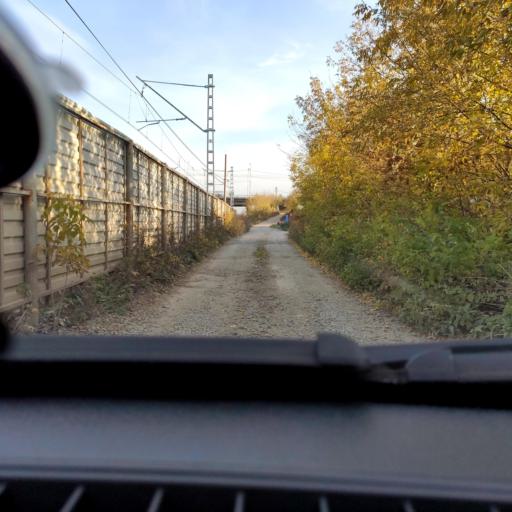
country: RU
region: Bashkortostan
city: Ufa
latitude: 54.7406
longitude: 55.9291
